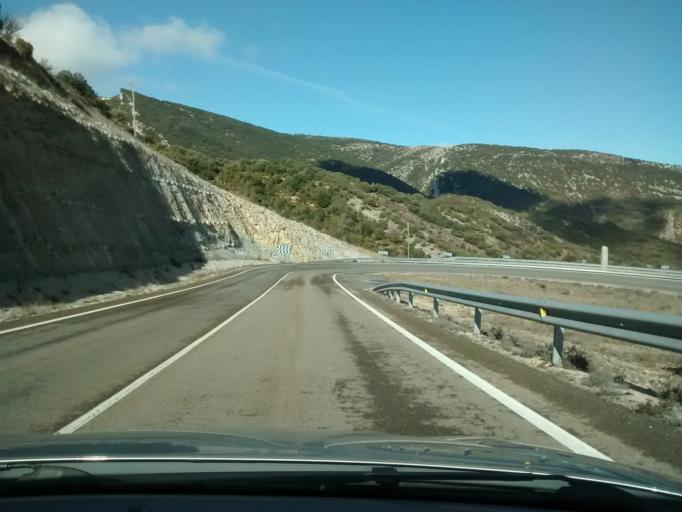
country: ES
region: Castille and Leon
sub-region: Provincia de Burgos
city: Rucandio
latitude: 42.8391
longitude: -3.6107
